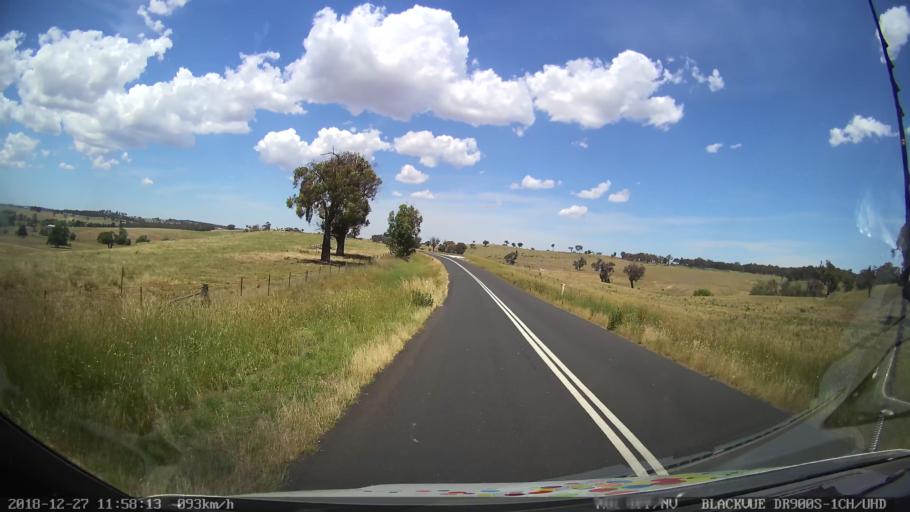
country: AU
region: New South Wales
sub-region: Blayney
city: Blayney
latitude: -33.7212
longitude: 149.3851
